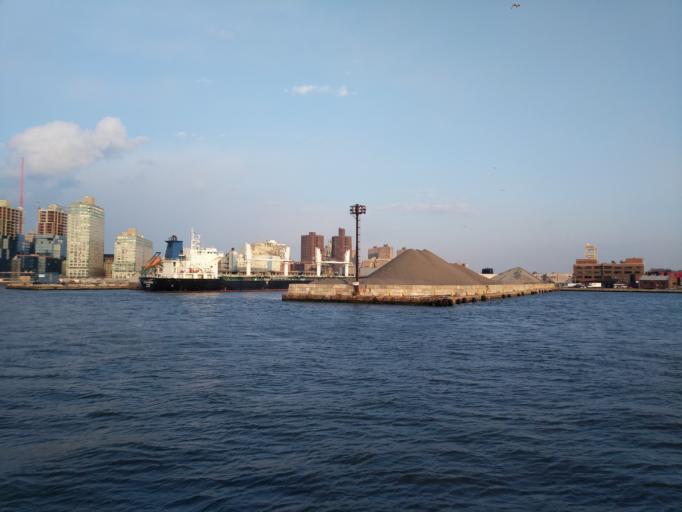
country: US
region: New York
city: New York City
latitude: 40.7081
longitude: -73.9759
